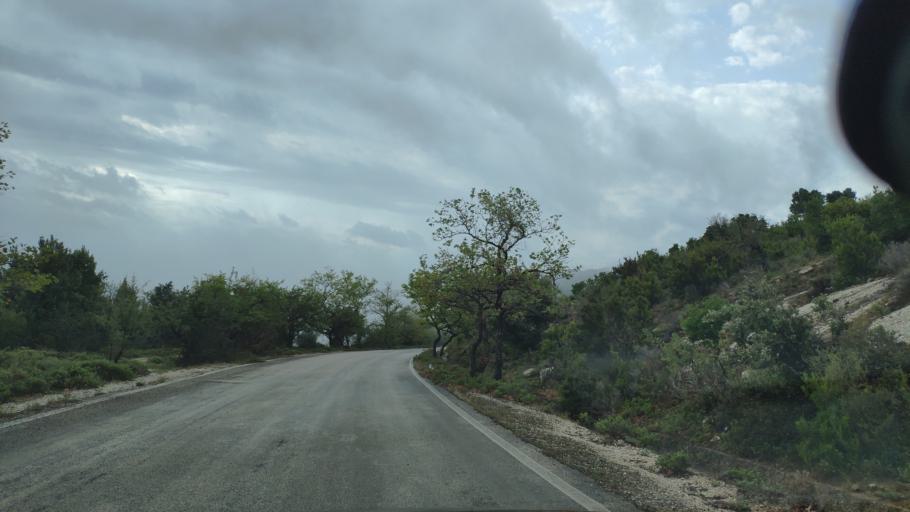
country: GR
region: West Greece
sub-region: Nomos Aitolias kai Akarnanias
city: Sardinia
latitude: 38.8513
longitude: 21.3151
